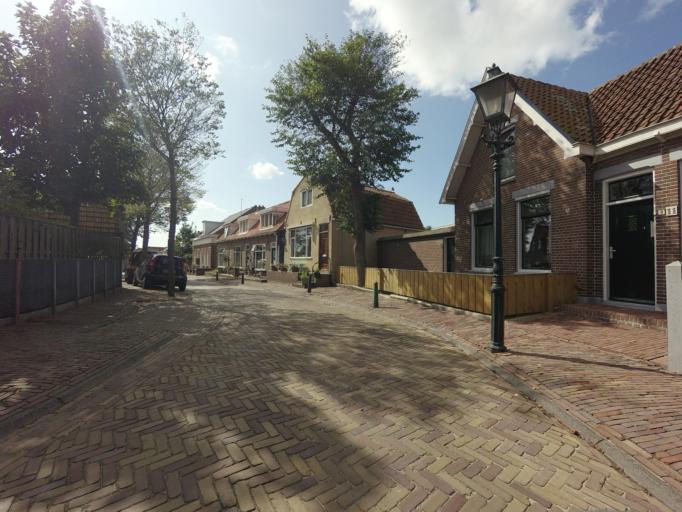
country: NL
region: Friesland
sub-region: Gemeente Terschelling
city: West-Terschelling
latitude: 53.3602
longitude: 5.2128
